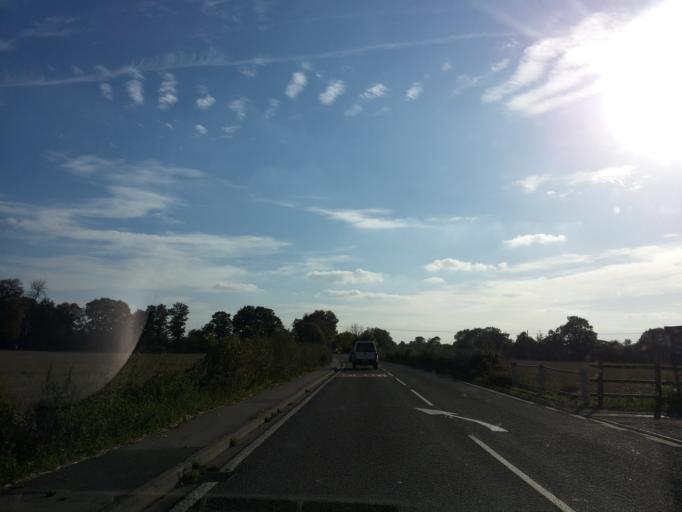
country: GB
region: England
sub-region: East Riding of Yorkshire
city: Snaith
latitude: 53.7015
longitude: -1.0225
